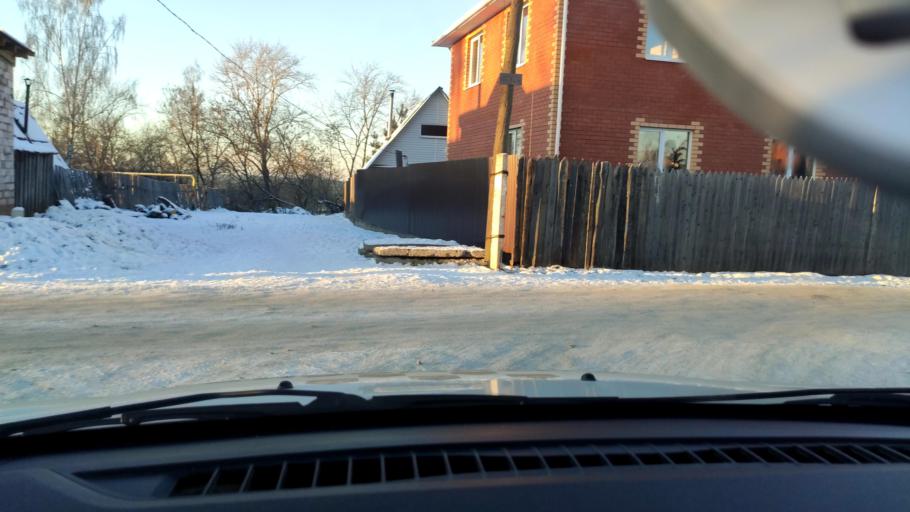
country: RU
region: Perm
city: Perm
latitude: 58.0529
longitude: 56.3330
